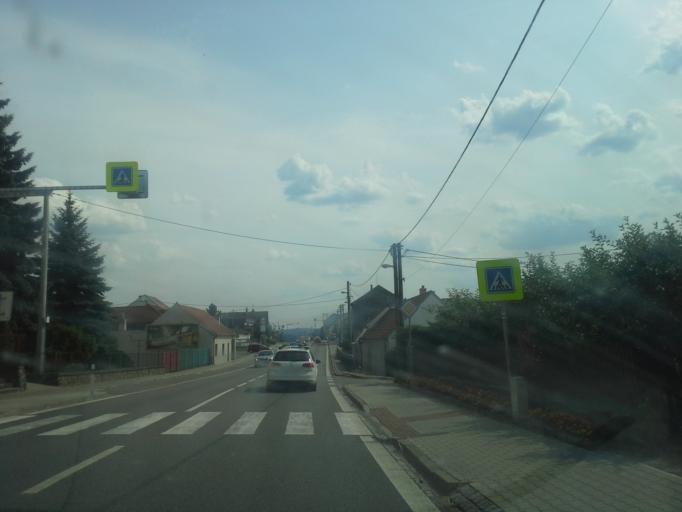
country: CZ
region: South Moravian
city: Lipuvka
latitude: 49.3403
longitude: 16.5529
